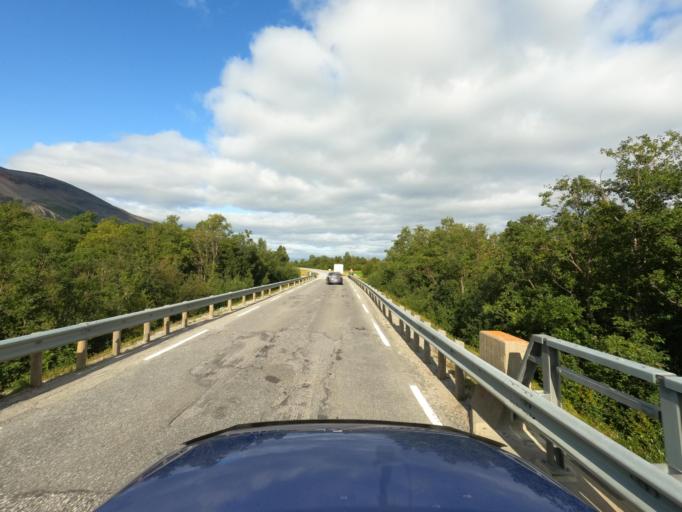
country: NO
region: Finnmark Fylke
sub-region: Porsanger
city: Lakselv
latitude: 70.0659
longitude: 24.9291
